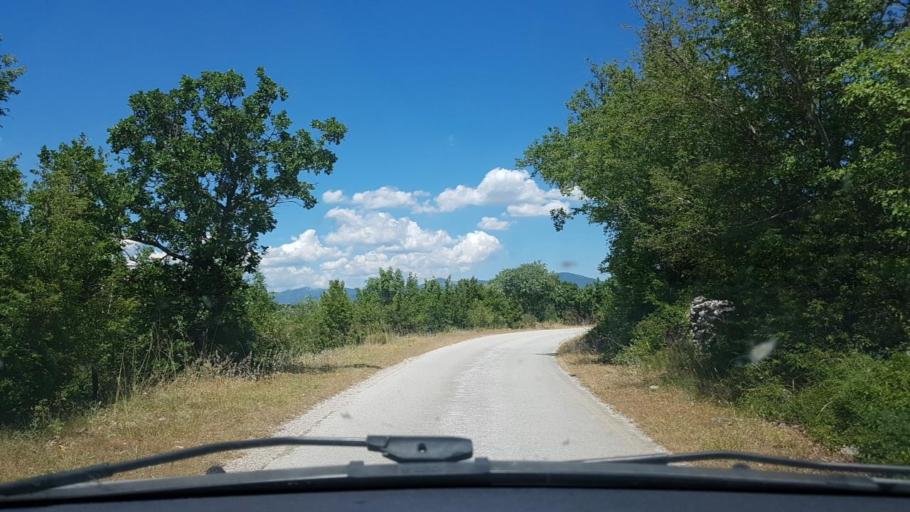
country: HR
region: Sibensko-Kniniska
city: Kistanje
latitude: 44.0028
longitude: 16.0303
